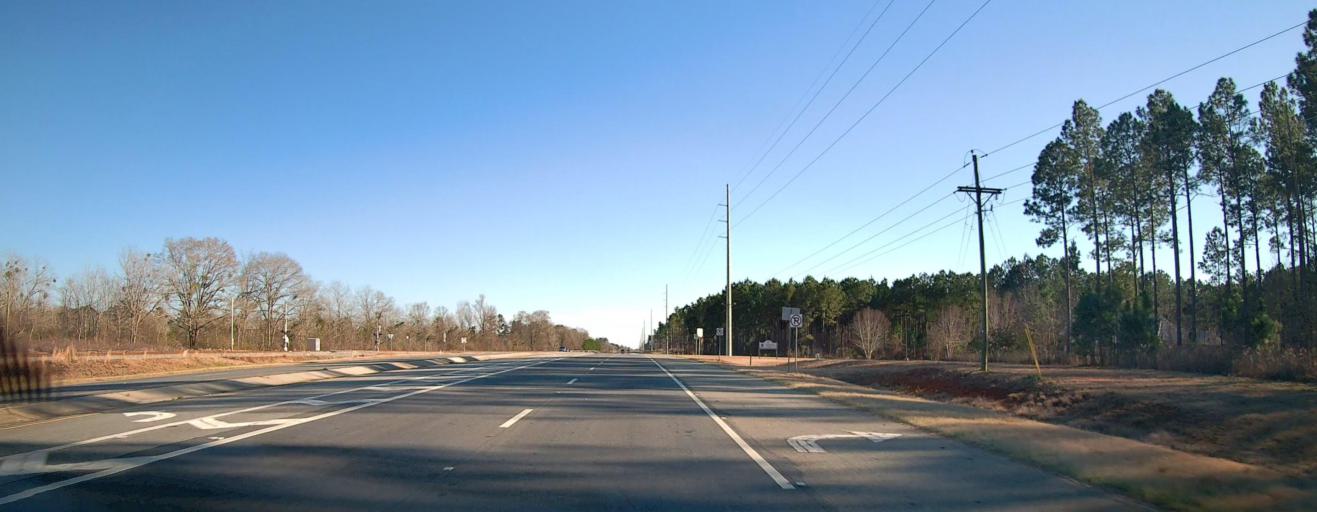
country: US
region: Georgia
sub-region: Lee County
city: Leesburg
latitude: 31.8761
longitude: -84.2407
